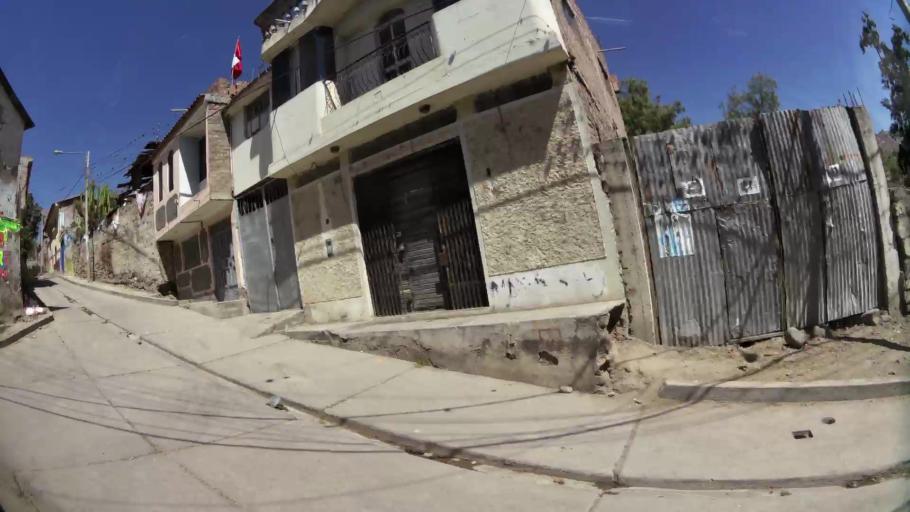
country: PE
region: Ayacucho
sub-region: Provincia de Huamanga
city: Carmen Alto
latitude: -13.1744
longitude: -74.2265
